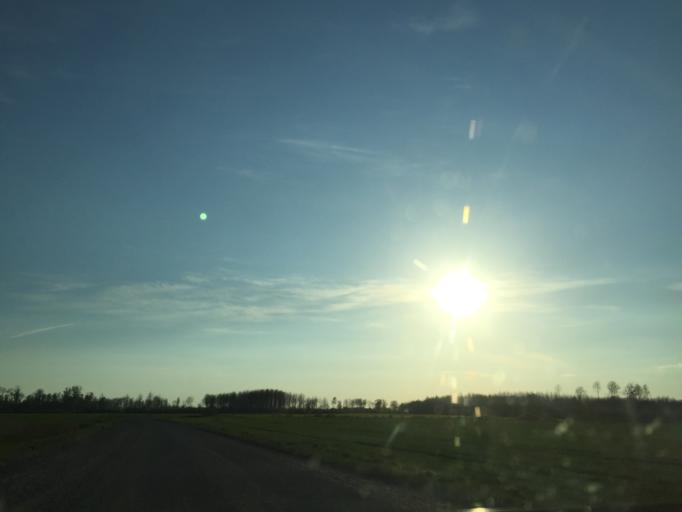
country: LV
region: Bauskas Rajons
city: Bauska
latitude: 56.2834
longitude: 24.2598
